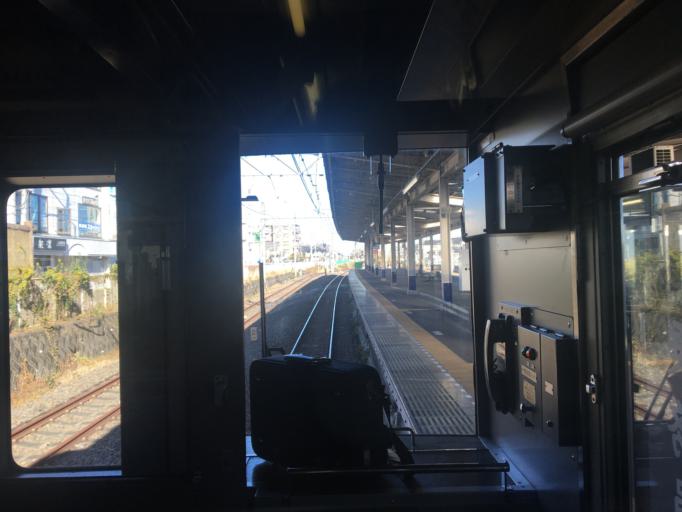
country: JP
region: Saitama
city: Sakado
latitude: 36.0035
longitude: 139.3974
